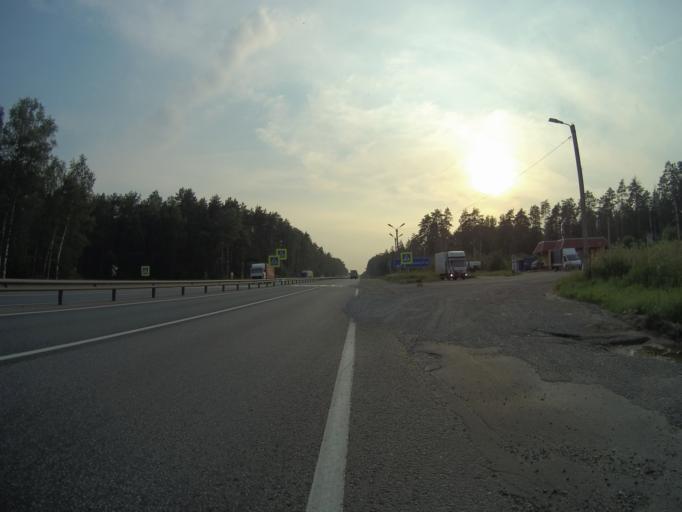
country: RU
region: Vladimir
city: Kameshkovo
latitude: 56.1964
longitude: 40.9926
